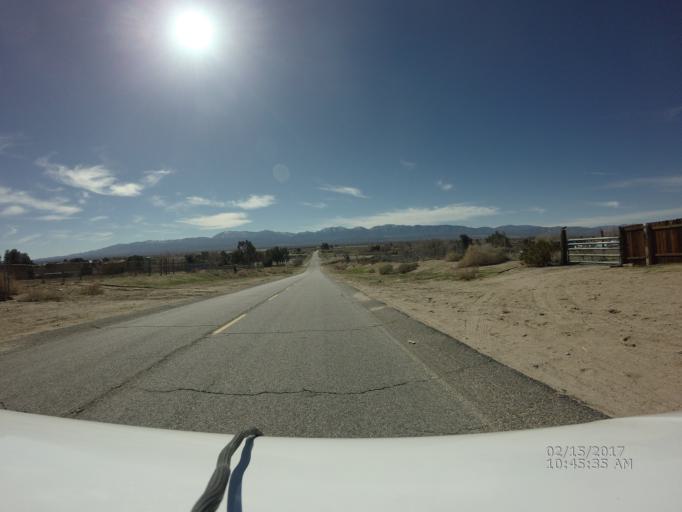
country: US
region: California
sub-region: Los Angeles County
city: Lake Los Angeles
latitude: 34.5861
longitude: -117.8533
